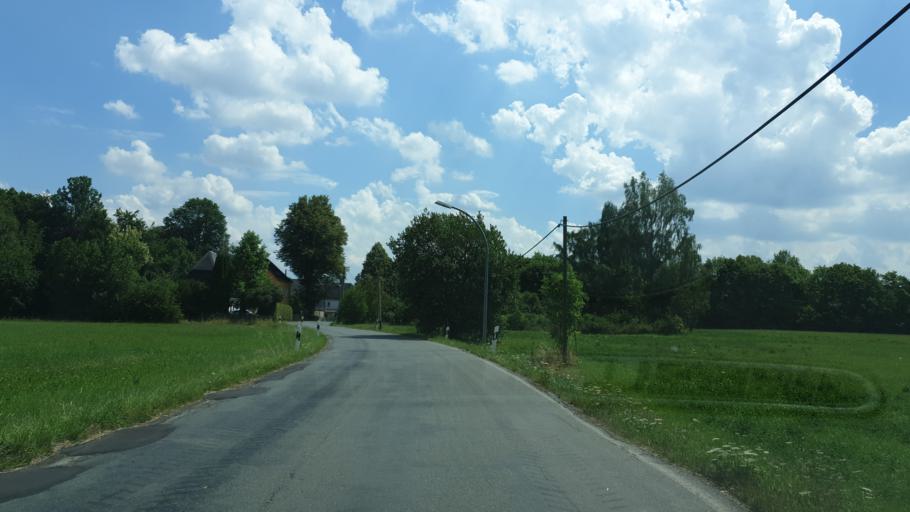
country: DE
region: Saxony
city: Kirchberg
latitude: 50.7956
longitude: 12.7840
